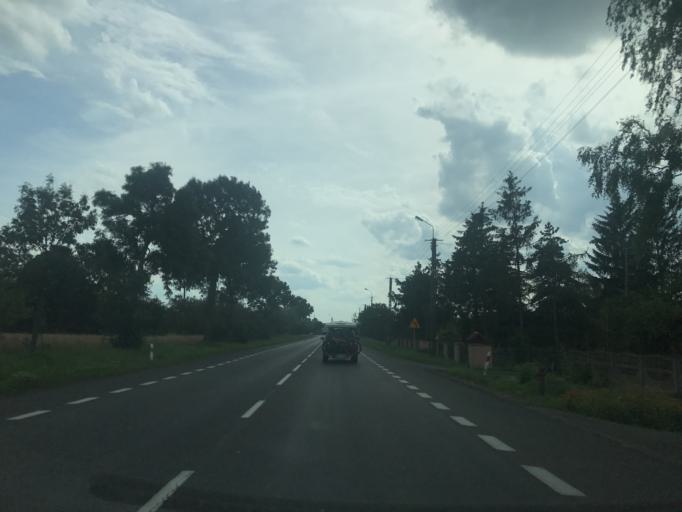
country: PL
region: Masovian Voivodeship
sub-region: Powiat mlawski
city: Wisniewo
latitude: 53.0055
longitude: 20.3298
